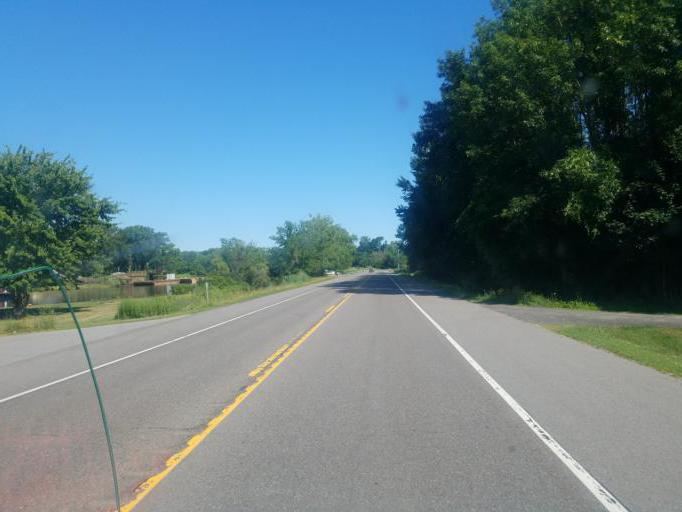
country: US
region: New York
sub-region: Wayne County
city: Lyons
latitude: 43.0614
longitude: -77.0188
